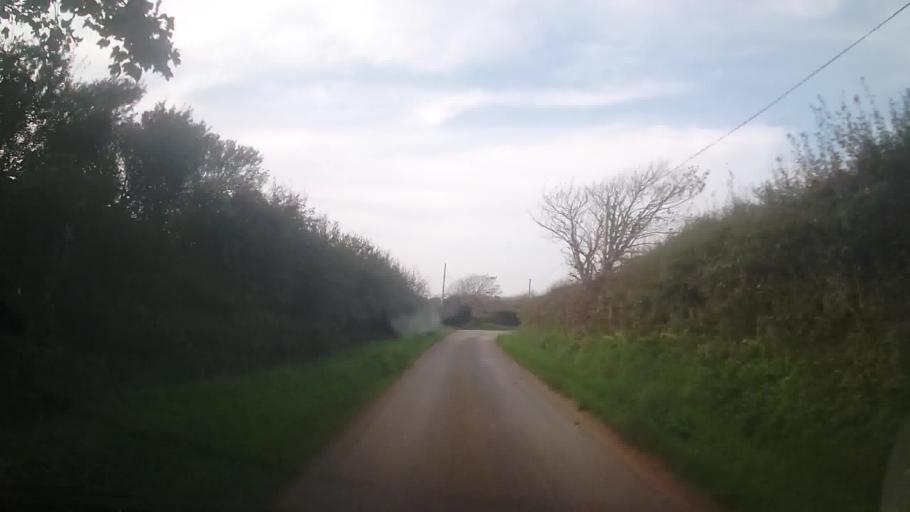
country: GB
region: Wales
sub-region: Pembrokeshire
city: Camrose
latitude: 51.8865
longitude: -5.0550
